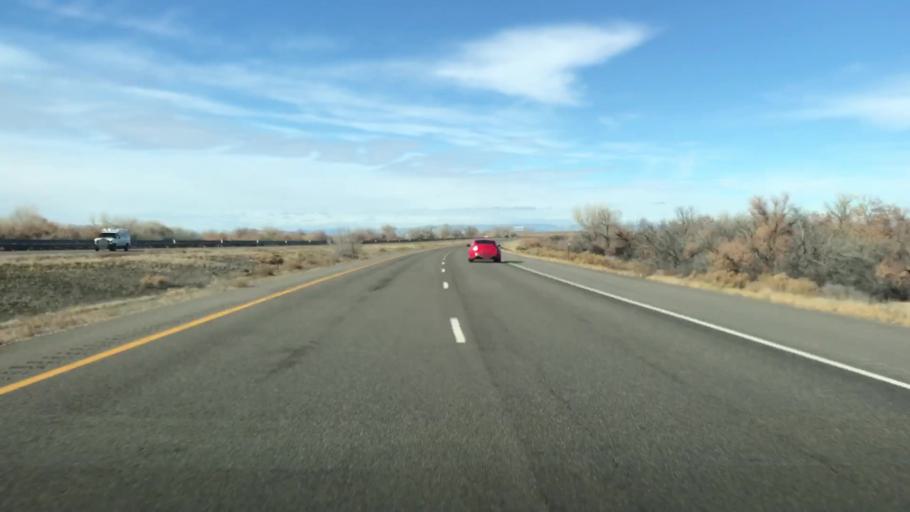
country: US
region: Colorado
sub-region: Mesa County
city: Redlands
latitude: 39.1211
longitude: -108.6761
